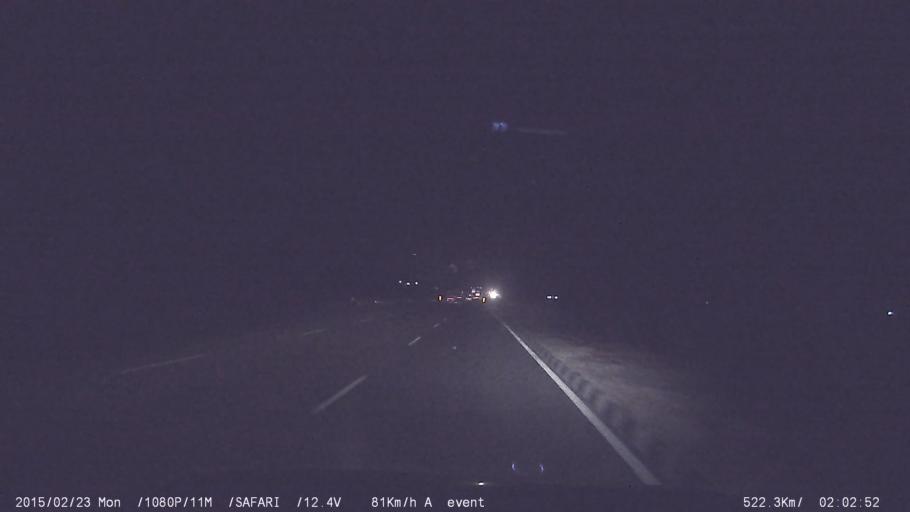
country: IN
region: Tamil Nadu
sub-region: Krishnagiri
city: Krishnagiri
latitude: 12.6409
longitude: 78.0599
